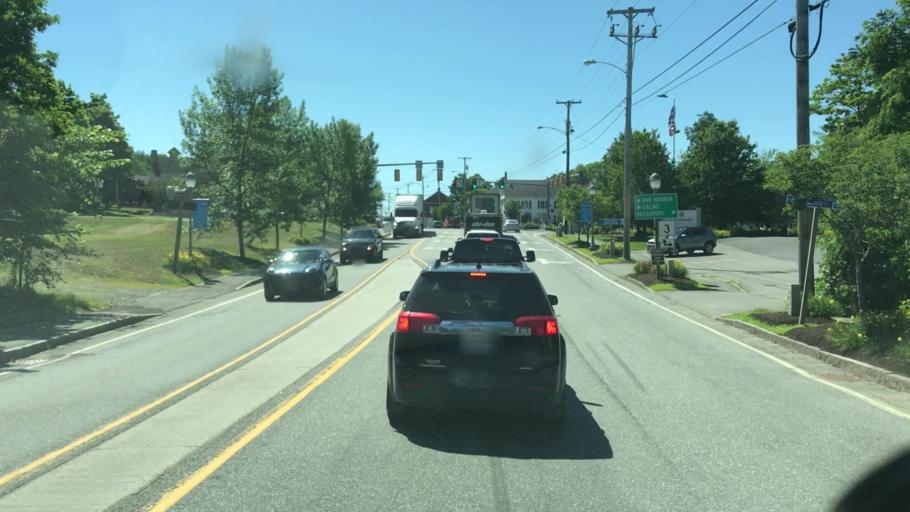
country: US
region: Maine
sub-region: Hancock County
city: Ellsworth
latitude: 44.5438
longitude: -68.4209
